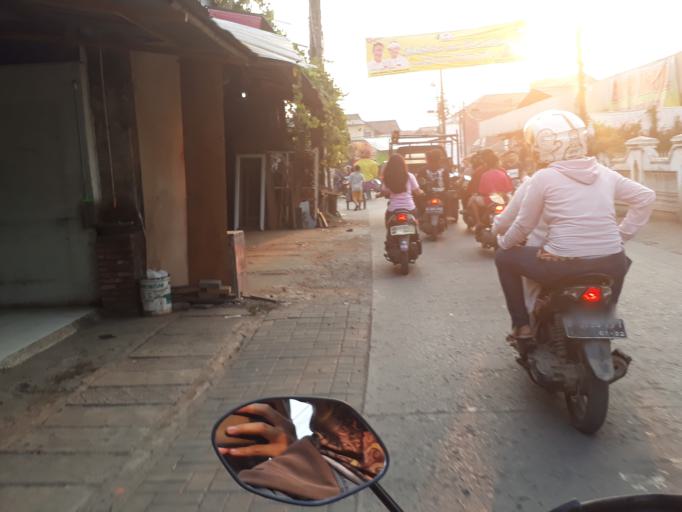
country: ID
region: West Java
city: Bekasi
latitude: -6.2429
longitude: 107.0424
